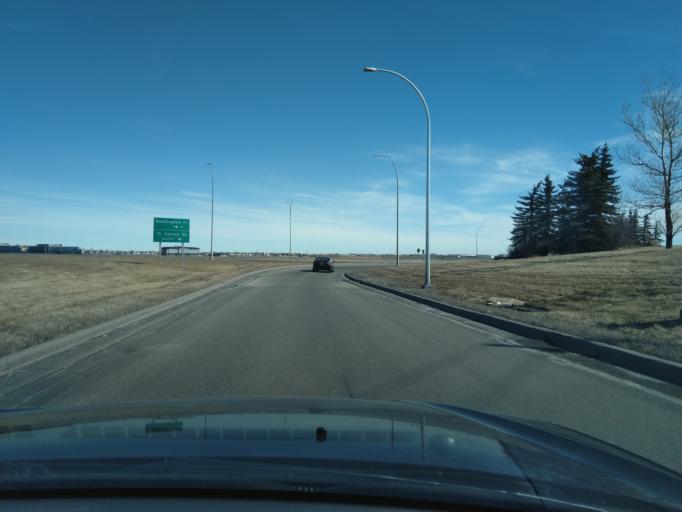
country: CA
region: Alberta
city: Calgary
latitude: 51.1326
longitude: -114.0698
